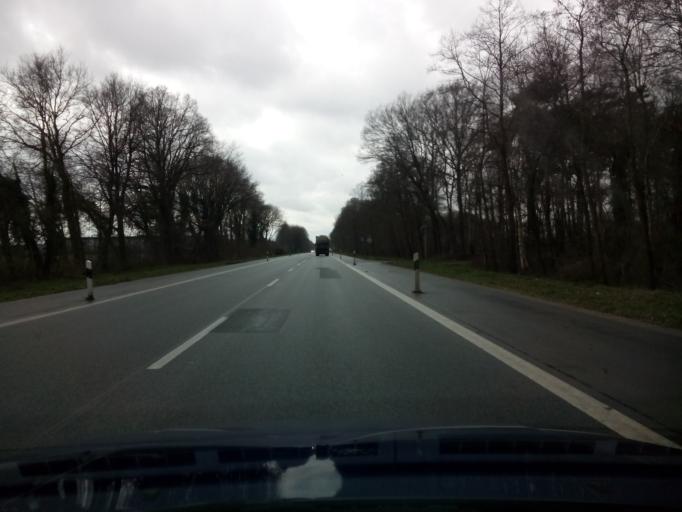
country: DE
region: Lower Saxony
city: Wildeshausen
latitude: 52.9404
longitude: 8.4753
